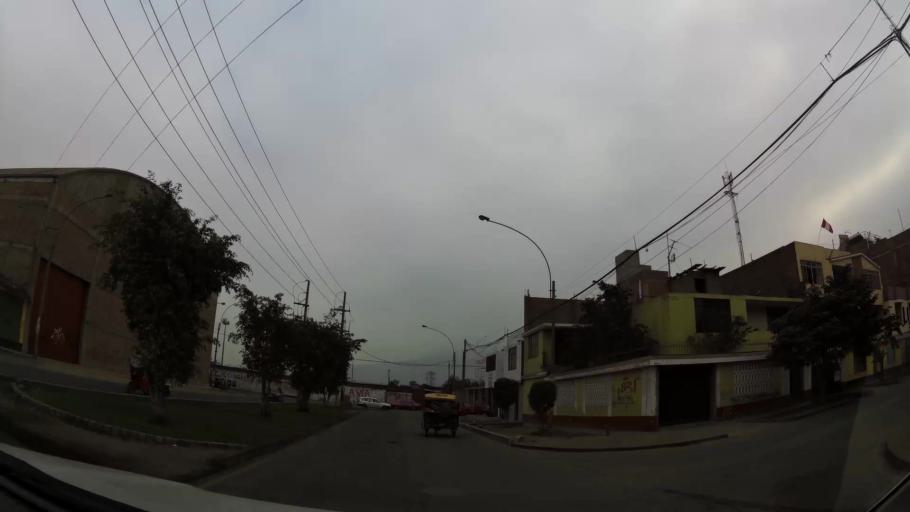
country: PE
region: Lima
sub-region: Lima
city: Independencia
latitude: -11.9769
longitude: -77.0047
